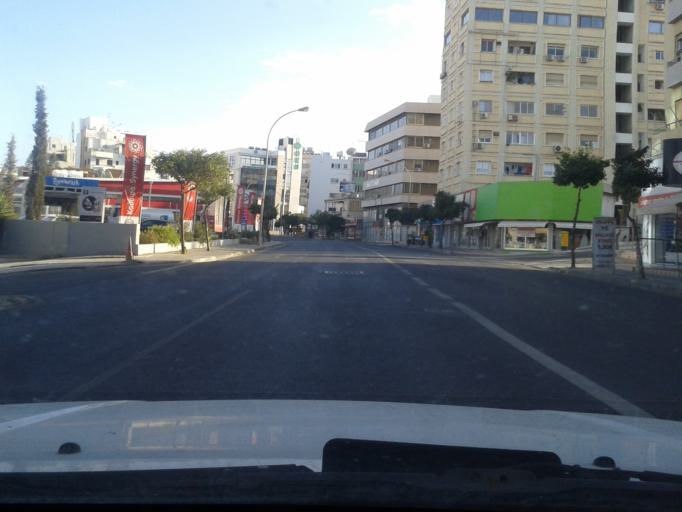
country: CY
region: Lefkosia
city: Nicosia
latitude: 35.1573
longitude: 33.3579
